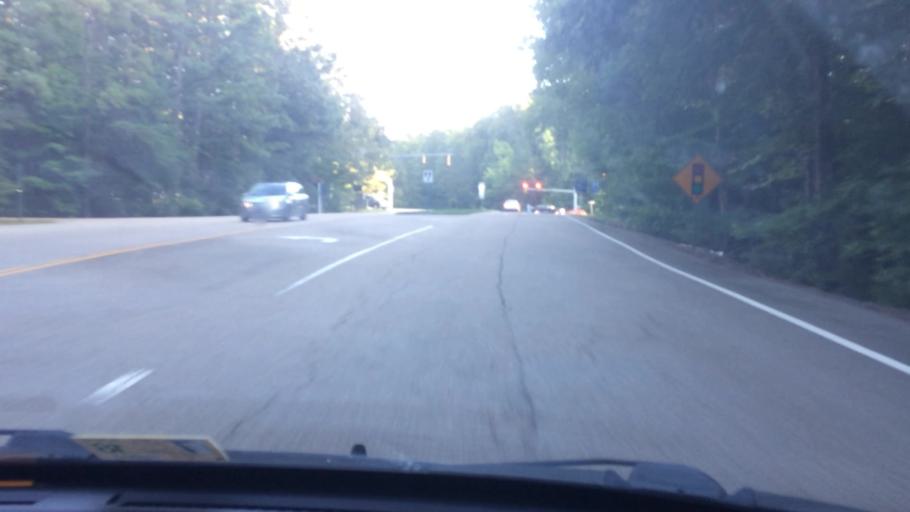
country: US
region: Virginia
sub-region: City of Williamsburg
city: Williamsburg
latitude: 37.2494
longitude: -76.7027
